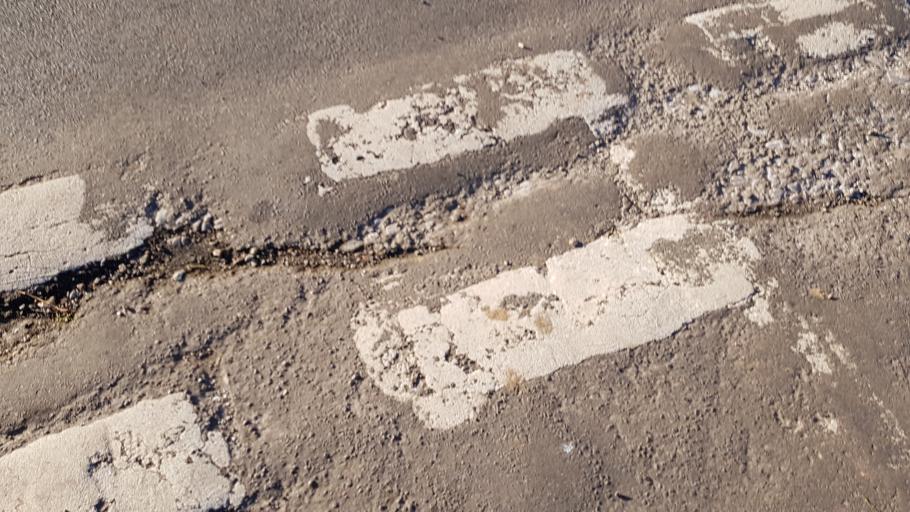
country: GB
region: England
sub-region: Somerset
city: Chard
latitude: 50.9045
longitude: -3.0021
